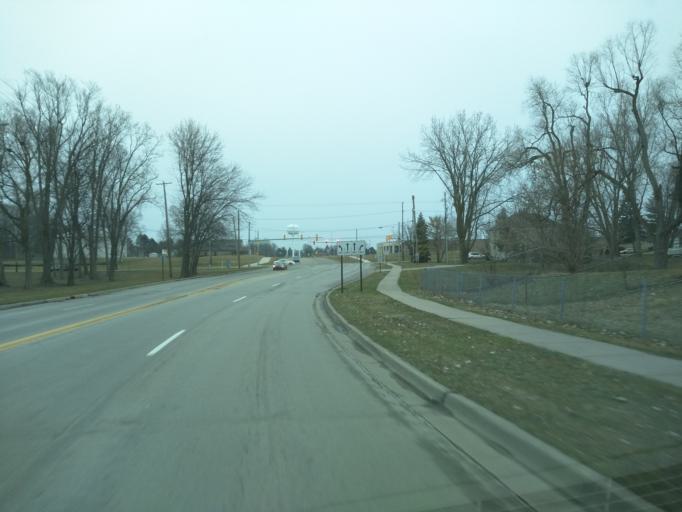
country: US
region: Michigan
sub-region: Eaton County
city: Waverly
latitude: 42.7350
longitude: -84.6203
